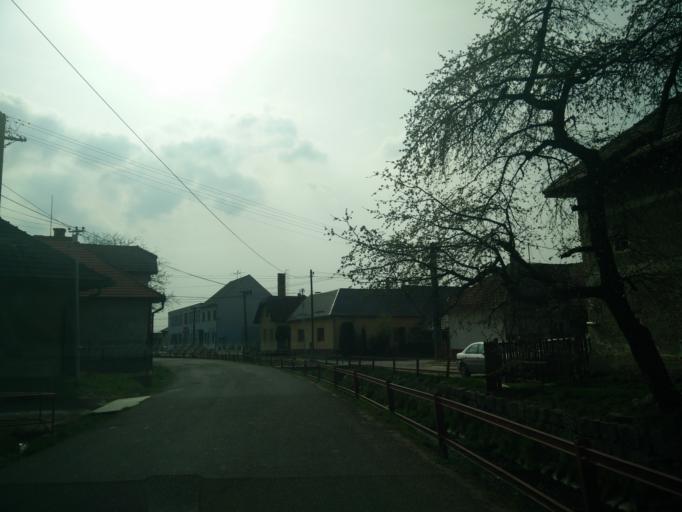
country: SK
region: Nitriansky
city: Prievidza
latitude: 48.8180
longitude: 18.6524
